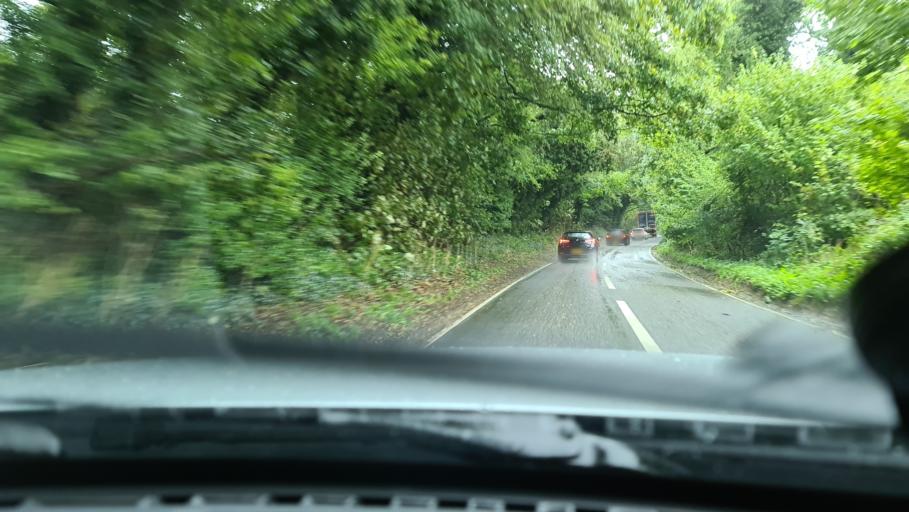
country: GB
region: England
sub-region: Oxfordshire
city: Woodstock
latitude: 51.8762
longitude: -1.3544
